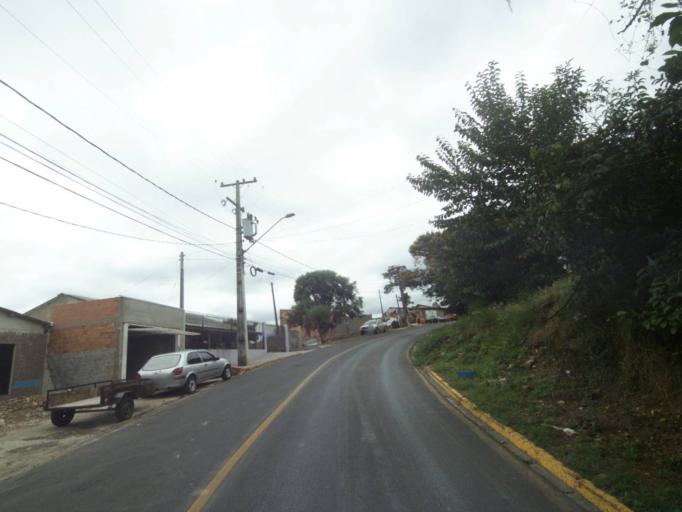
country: BR
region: Parana
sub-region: Telemaco Borba
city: Telemaco Borba
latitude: -24.3138
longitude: -50.6186
